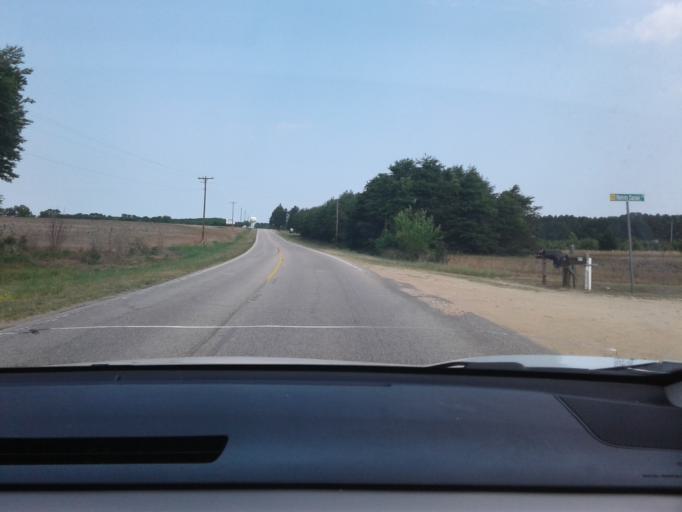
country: US
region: North Carolina
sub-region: Harnett County
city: Coats
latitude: 35.3867
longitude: -78.6647
